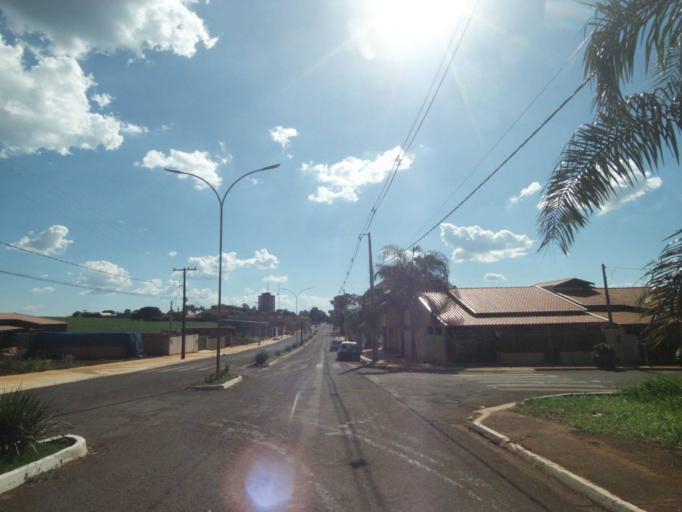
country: BR
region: Parana
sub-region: Sertanopolis
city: Sertanopolis
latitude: -23.0393
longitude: -50.8114
